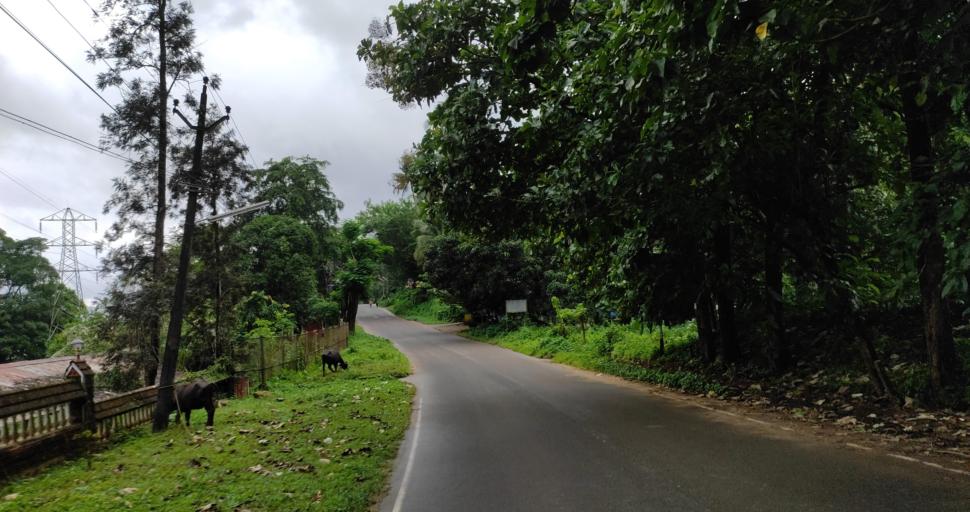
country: IN
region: Kerala
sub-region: Ernakulam
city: Angamali
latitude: 10.2908
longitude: 76.5479
